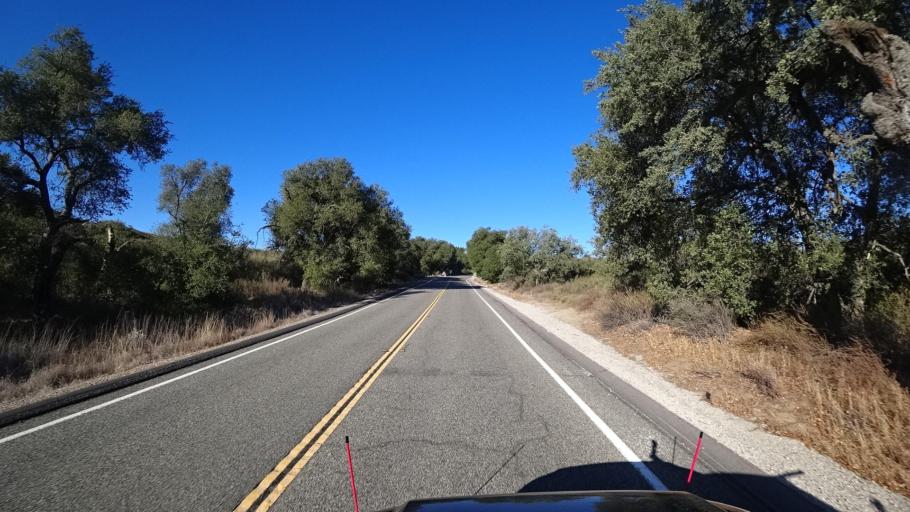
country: MX
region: Baja California
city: Tecate
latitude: 32.5996
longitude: -116.5772
